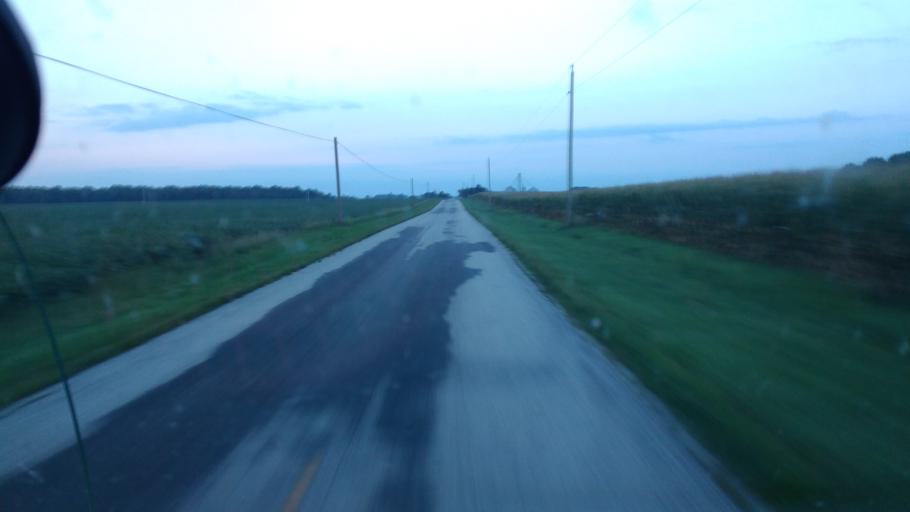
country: US
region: Ohio
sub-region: Hardin County
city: Kenton
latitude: 40.6722
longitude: -83.5005
